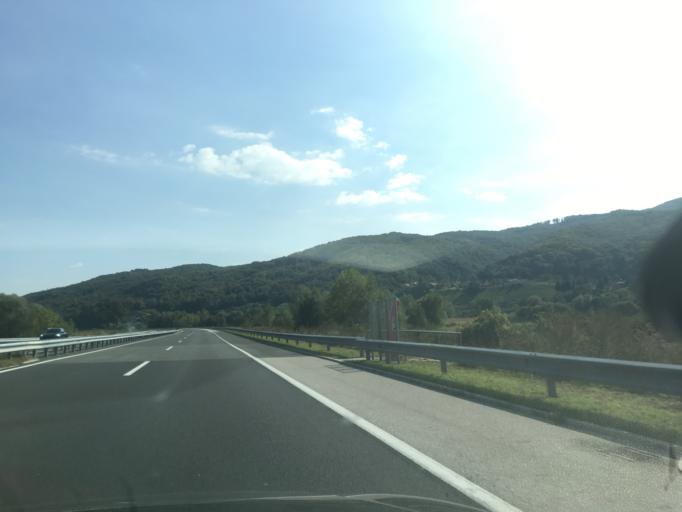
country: SI
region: Brezice
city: Brezice
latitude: 45.8841
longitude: 15.6195
